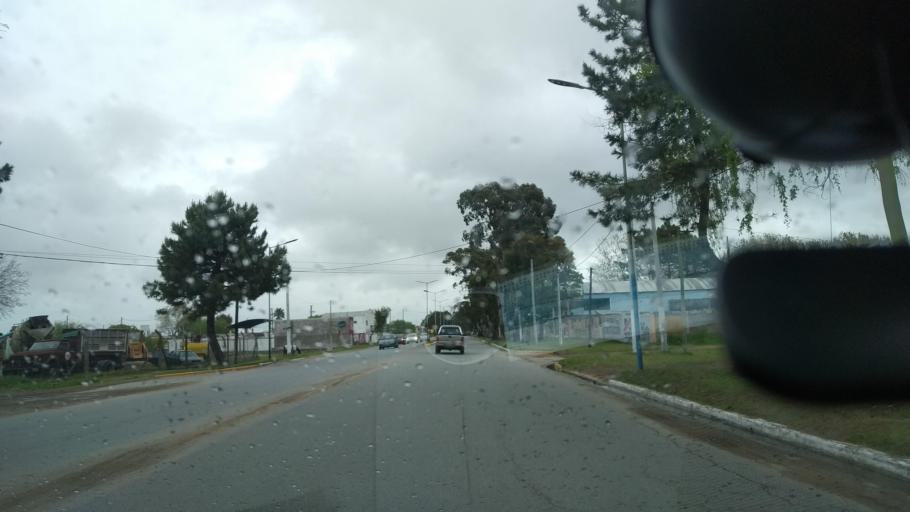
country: AR
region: Buenos Aires
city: San Clemente del Tuyu
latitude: -36.3825
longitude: -56.7232
